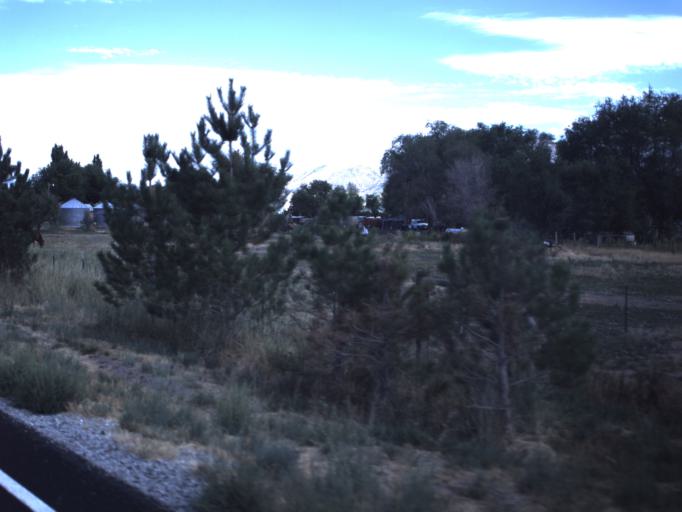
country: US
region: Utah
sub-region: Box Elder County
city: Honeyville
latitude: 41.6392
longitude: -112.1295
